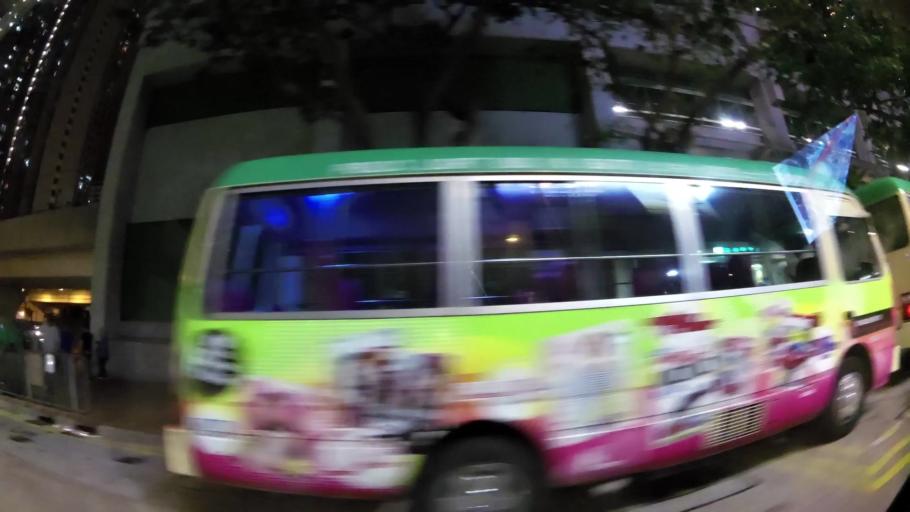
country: HK
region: Tsuen Wan
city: Tsuen Wan
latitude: 22.3577
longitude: 114.1281
